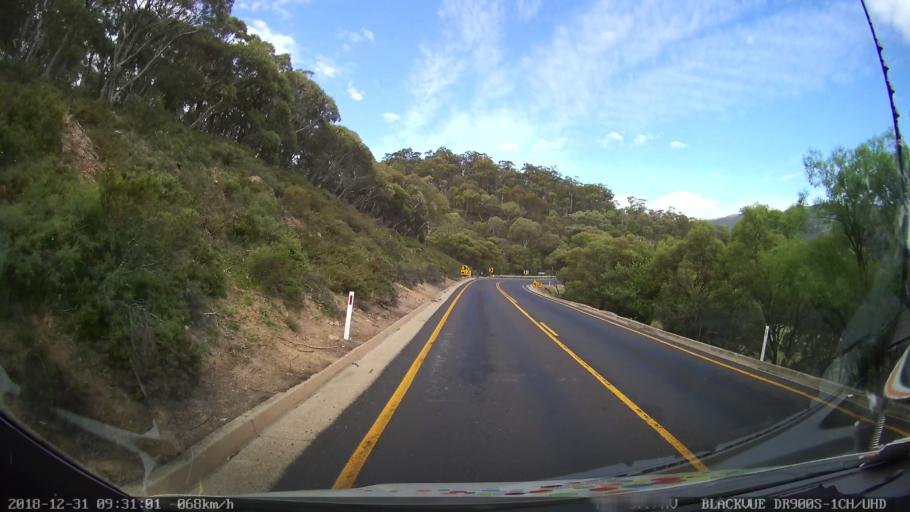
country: AU
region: New South Wales
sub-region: Snowy River
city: Jindabyne
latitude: -36.4507
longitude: 148.4477
